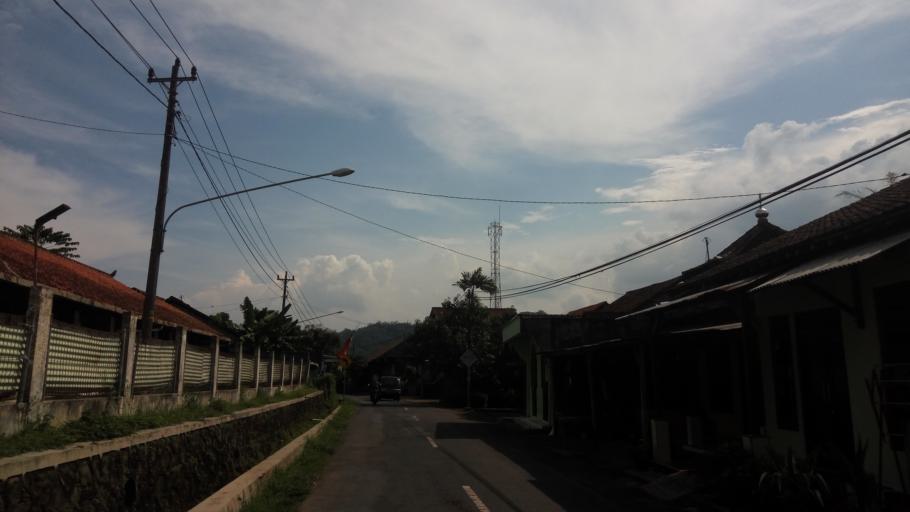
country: ID
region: Central Java
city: Ungaran
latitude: -7.1274
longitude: 110.4217
